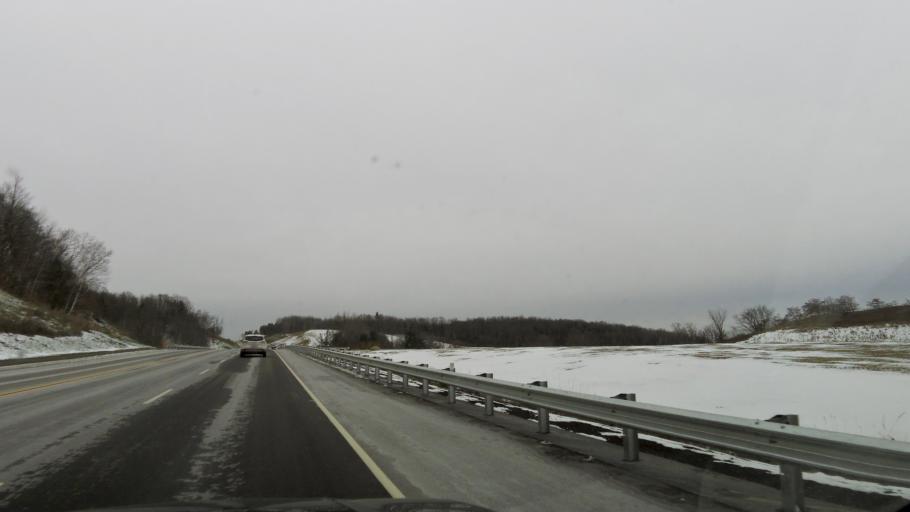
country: CA
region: Ontario
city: Newmarket
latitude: 44.0899
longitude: -79.5170
